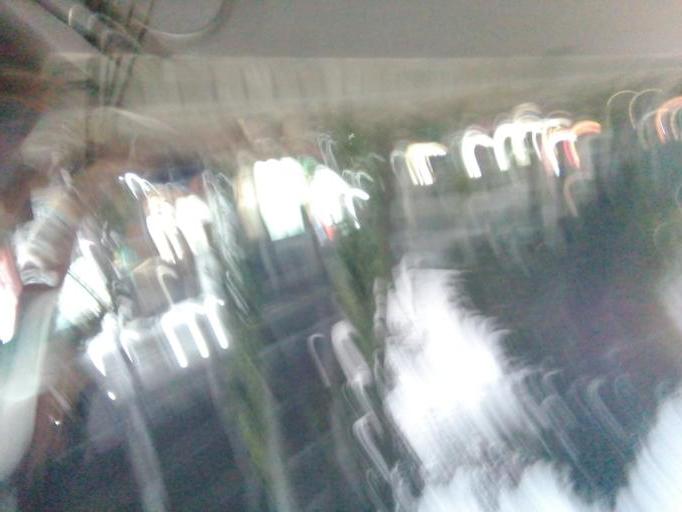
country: BD
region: Dhaka
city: Paltan
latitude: 23.7364
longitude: 90.4103
